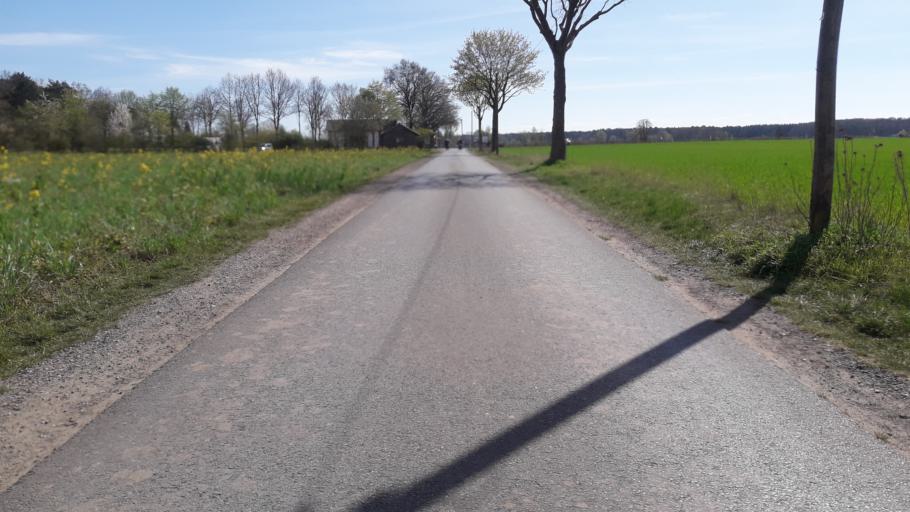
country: DE
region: North Rhine-Westphalia
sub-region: Regierungsbezirk Detmold
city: Delbruck
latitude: 51.7391
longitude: 8.5927
